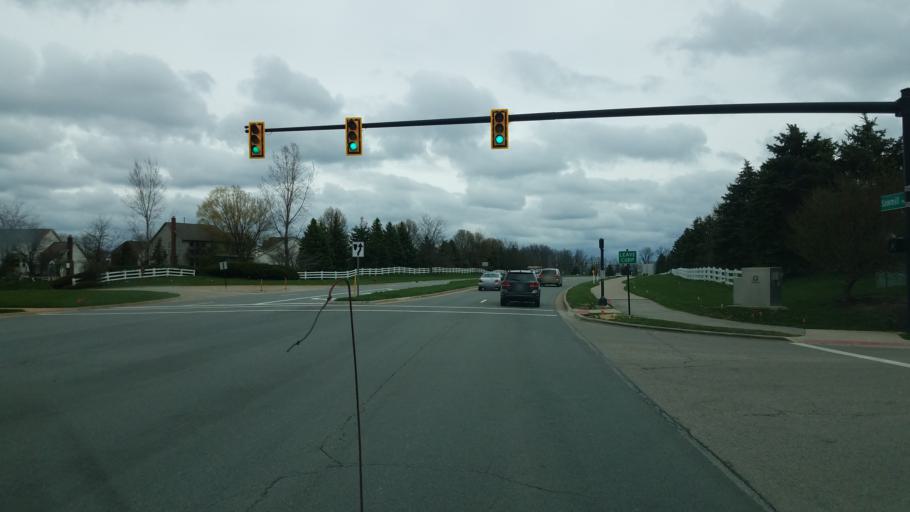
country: US
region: Ohio
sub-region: Delaware County
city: Powell
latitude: 40.1605
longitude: -83.0910
